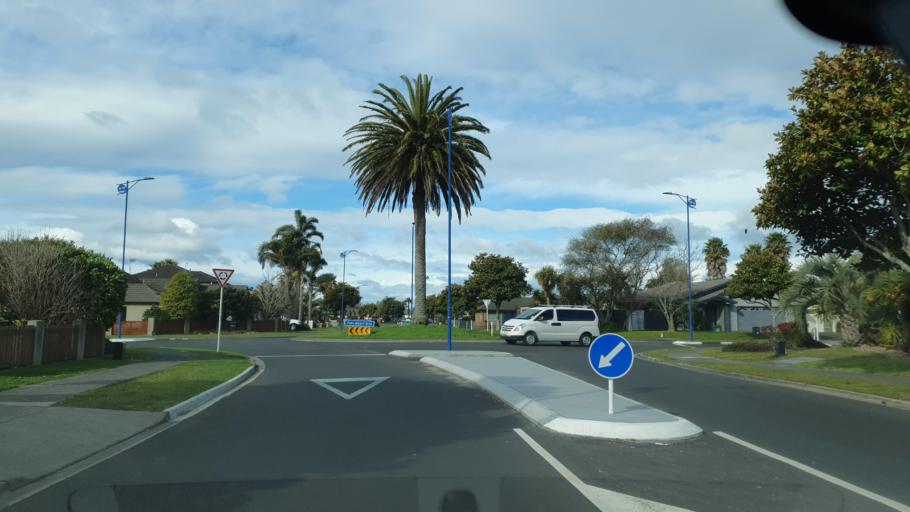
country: NZ
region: Bay of Plenty
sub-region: Tauranga City
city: Tauranga
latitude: -37.6992
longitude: 176.2709
